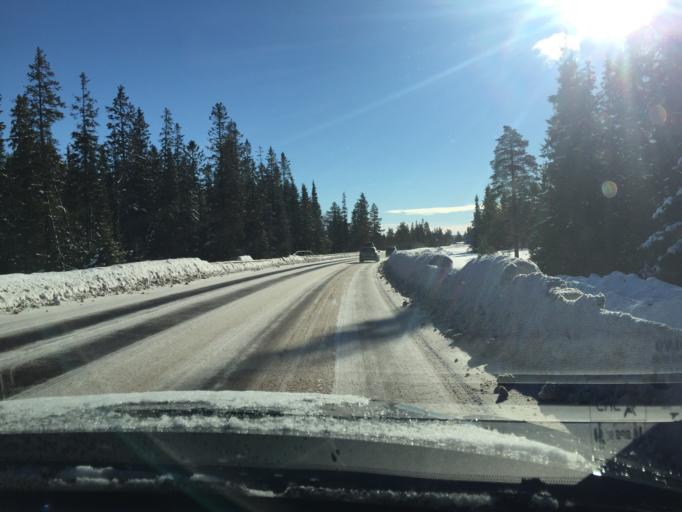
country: SE
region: Dalarna
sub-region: Malung-Saelens kommun
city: Malung
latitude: 61.1686
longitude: 13.1897
